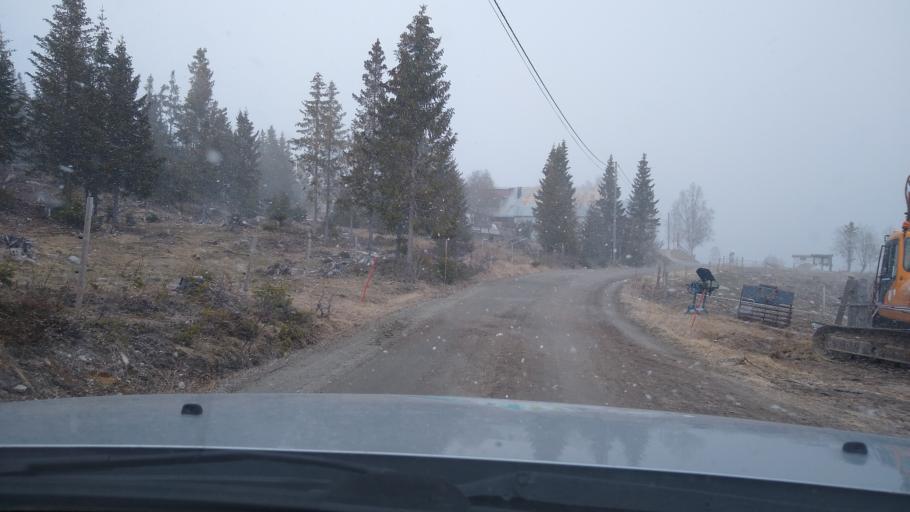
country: NO
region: Oppland
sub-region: Oyer
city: Tretten
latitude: 61.4631
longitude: 10.3444
